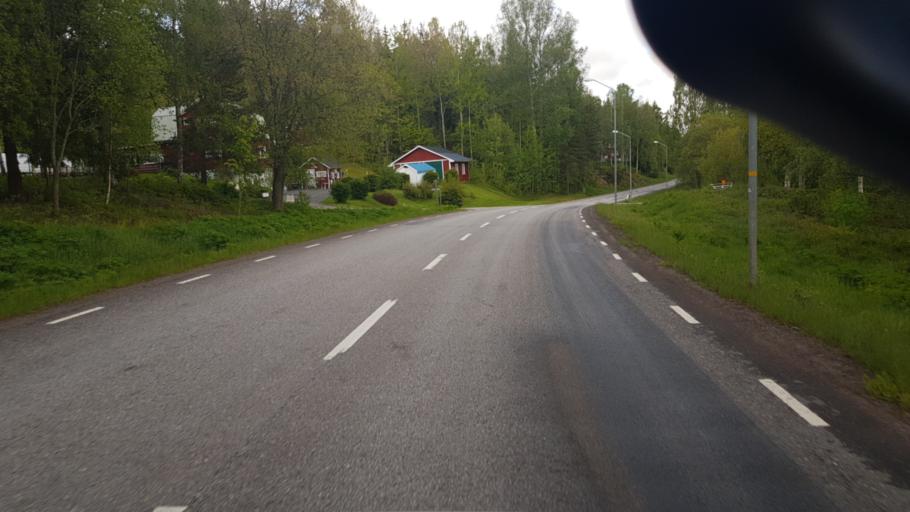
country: SE
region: Vaermland
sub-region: Eda Kommun
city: Amotfors
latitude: 59.7149
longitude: 12.1607
